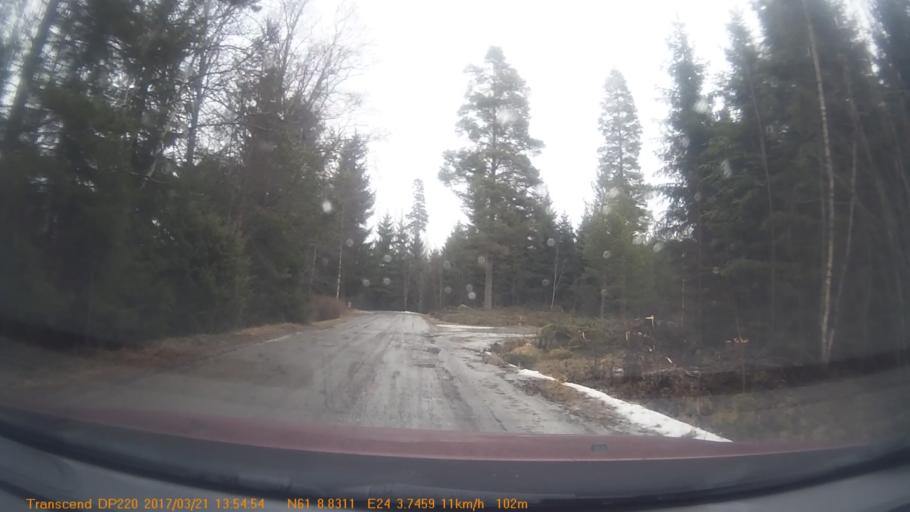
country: FI
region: Haeme
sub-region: Haemeenlinna
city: Kalvola
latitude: 61.1472
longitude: 24.0623
